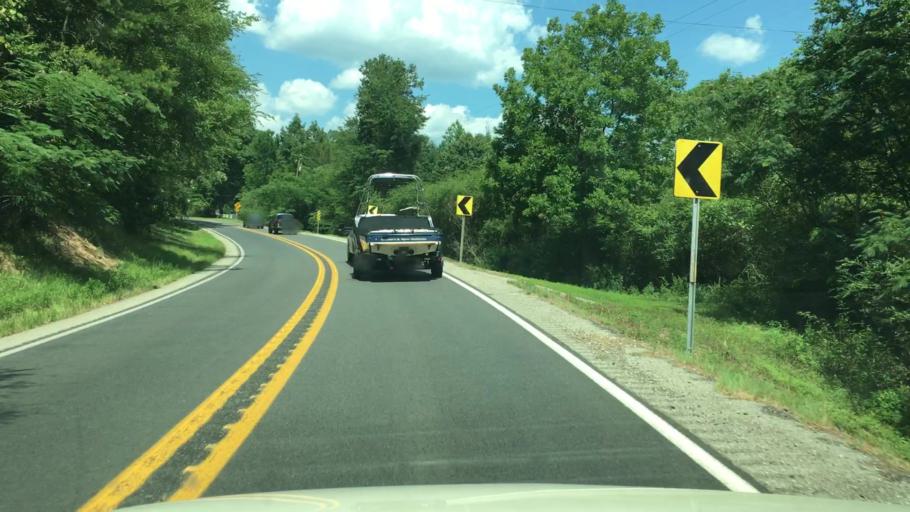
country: US
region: Arkansas
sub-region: Garland County
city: Lake Hamilton
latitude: 34.3867
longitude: -93.1228
